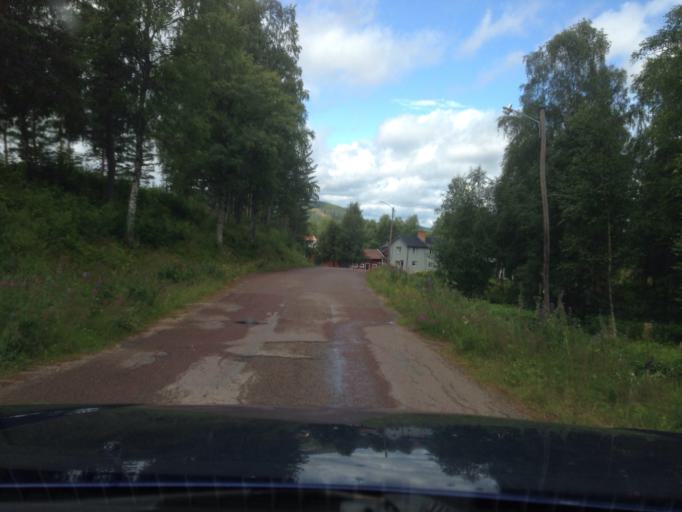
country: SE
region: Dalarna
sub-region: Vansbro Kommun
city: Jarna
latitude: 60.3276
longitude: 14.5378
